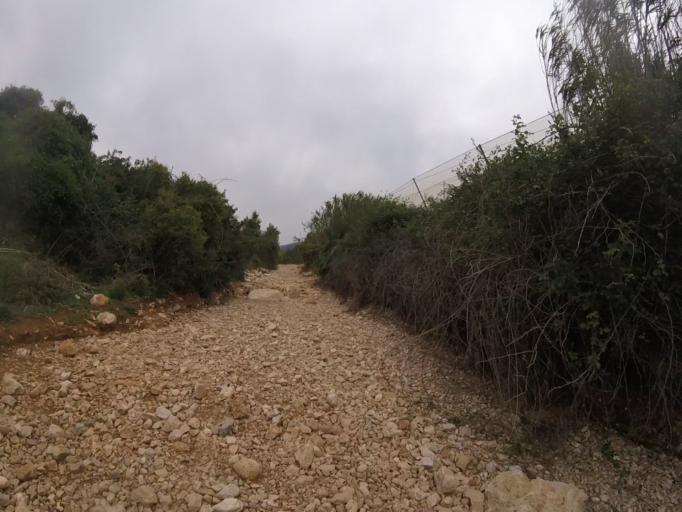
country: ES
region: Valencia
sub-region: Provincia de Castello
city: Alcala de Xivert
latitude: 40.2784
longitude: 0.2567
